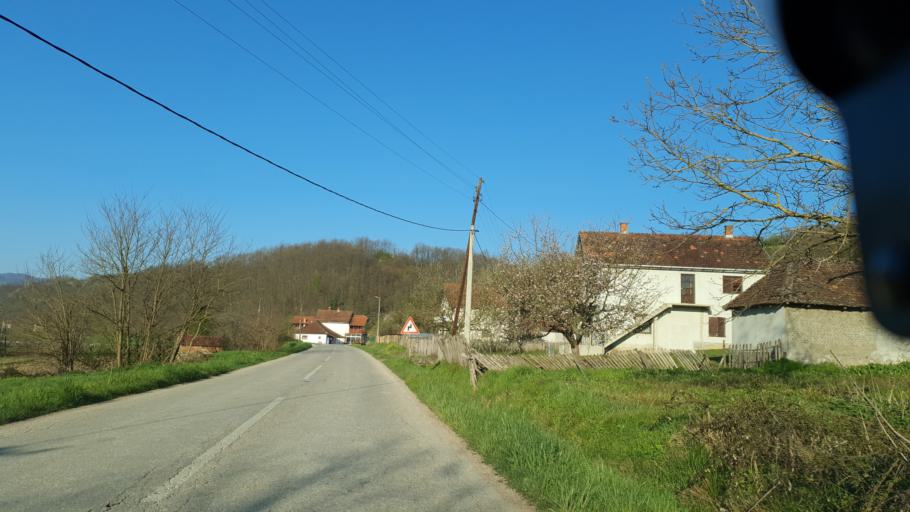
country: RS
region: Central Serbia
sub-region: Kolubarski Okrug
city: Osecina
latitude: 44.3565
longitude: 19.5295
